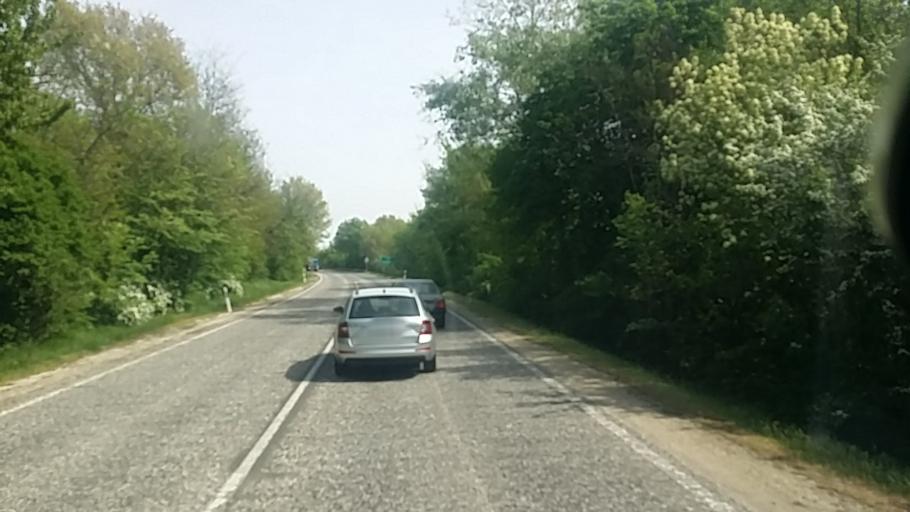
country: HU
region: Fejer
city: Etyek
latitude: 47.4867
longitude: 18.7707
